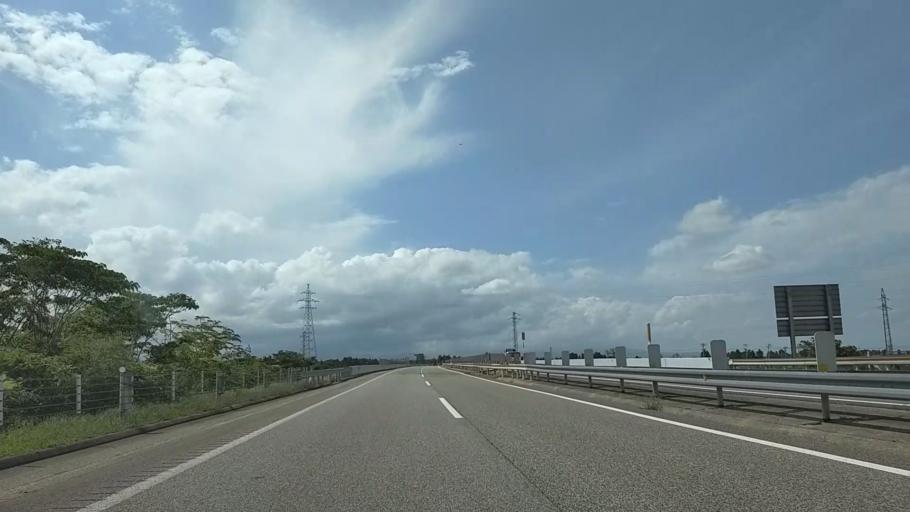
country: JP
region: Toyama
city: Kamiichi
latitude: 36.6805
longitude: 137.3201
